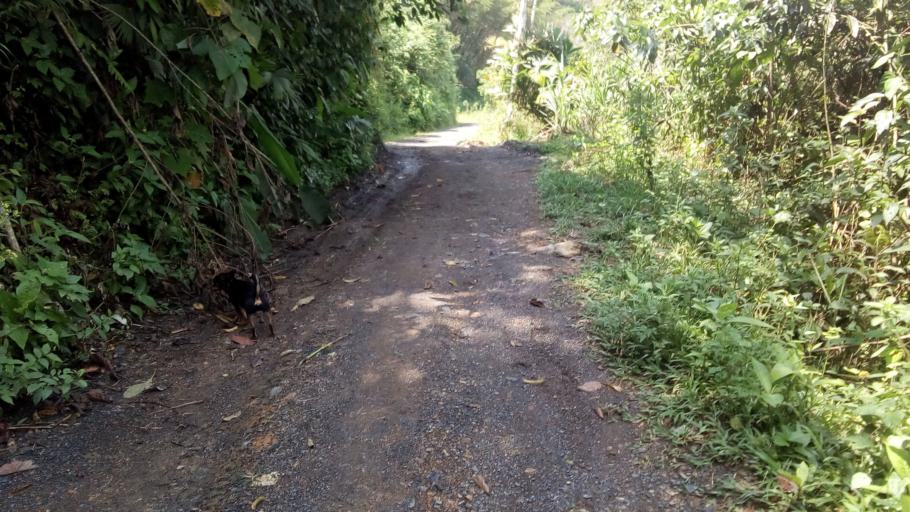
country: CO
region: Boyaca
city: Otanche
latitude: 5.6299
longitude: -74.2418
